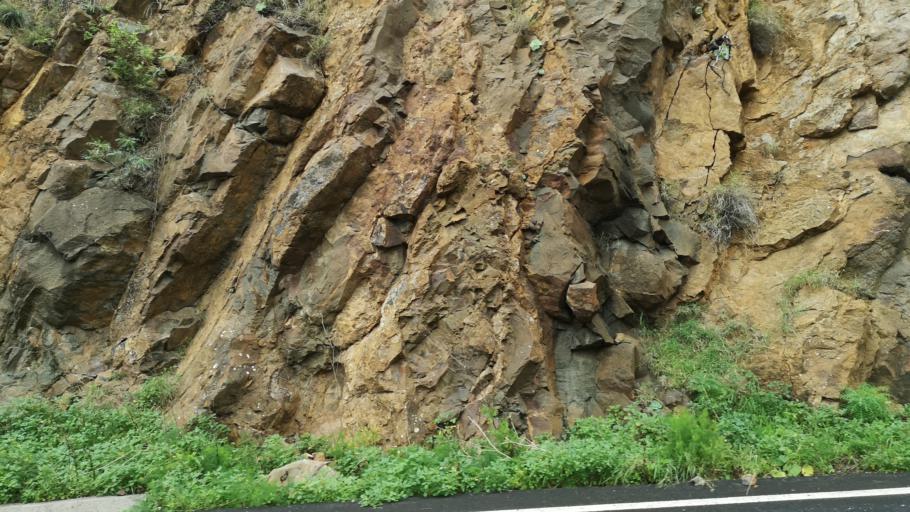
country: ES
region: Canary Islands
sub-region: Provincia de Santa Cruz de Tenerife
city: Agulo
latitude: 28.1866
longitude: -17.2123
